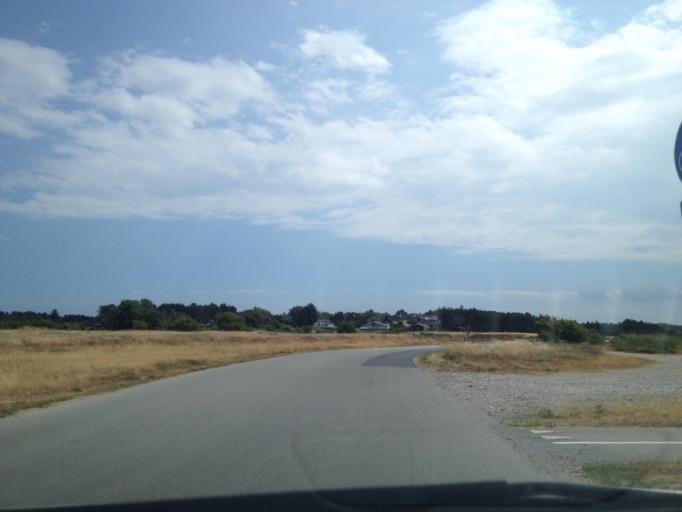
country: DK
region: Central Jutland
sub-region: Syddjurs Kommune
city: Ebeltoft
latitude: 56.1582
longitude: 10.6715
